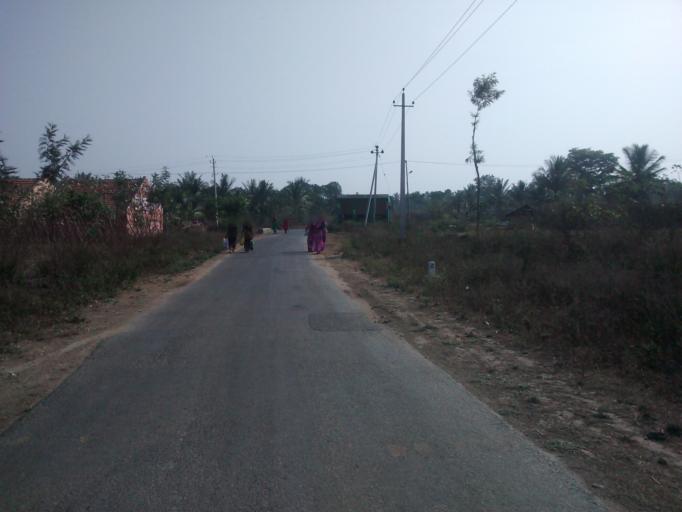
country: IN
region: Karnataka
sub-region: Hassan
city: Hassan
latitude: 12.9397
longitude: 76.1642
